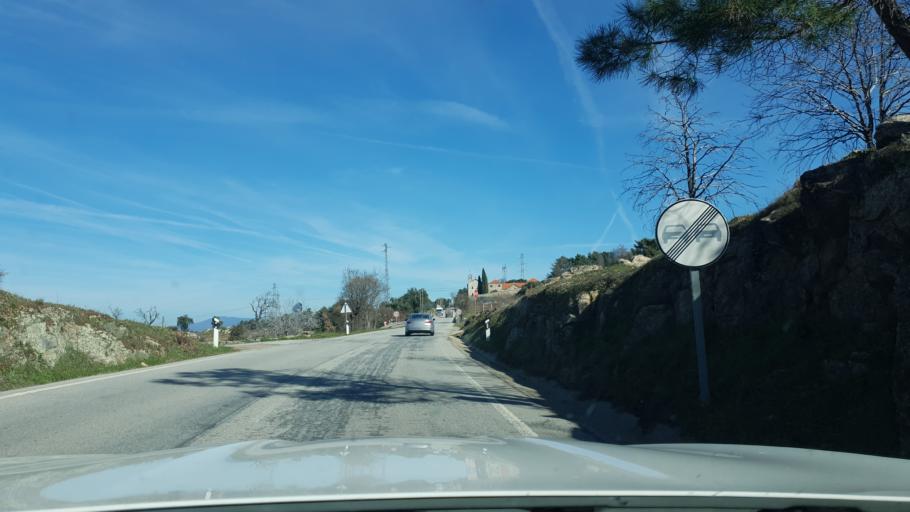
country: PT
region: Braganca
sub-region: Torre de Moncorvo
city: Torre de Moncorvo
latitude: 41.1842
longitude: -7.0233
